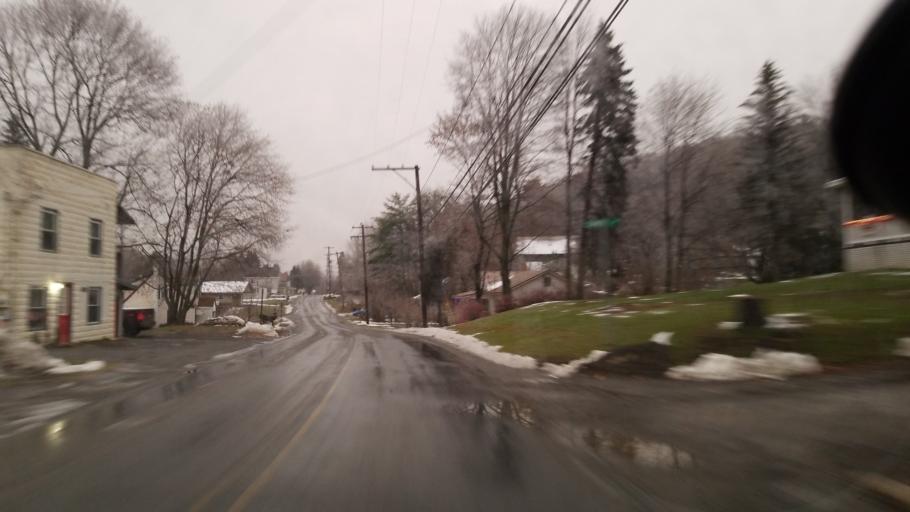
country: US
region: Pennsylvania
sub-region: Clearfield County
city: Clearfield
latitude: 41.0409
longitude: -78.4581
